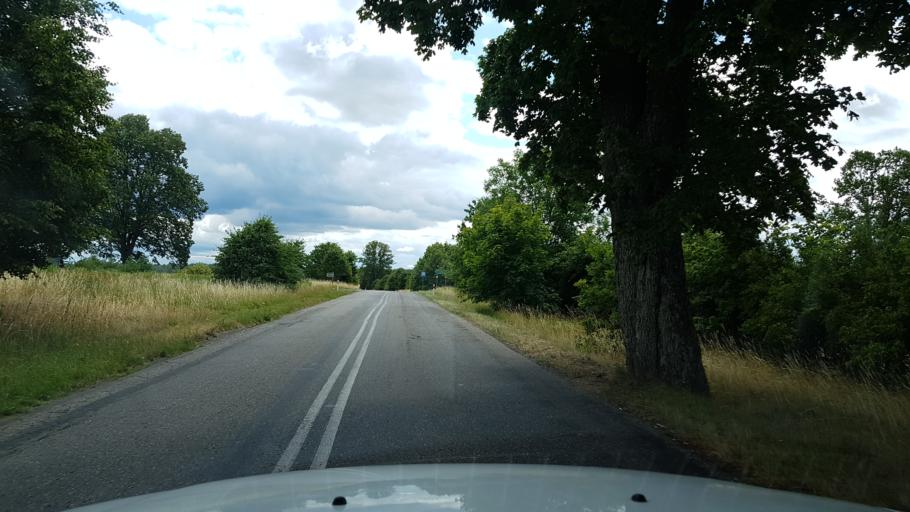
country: PL
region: West Pomeranian Voivodeship
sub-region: Powiat stargardzki
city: Insko
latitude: 53.3746
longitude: 15.5812
